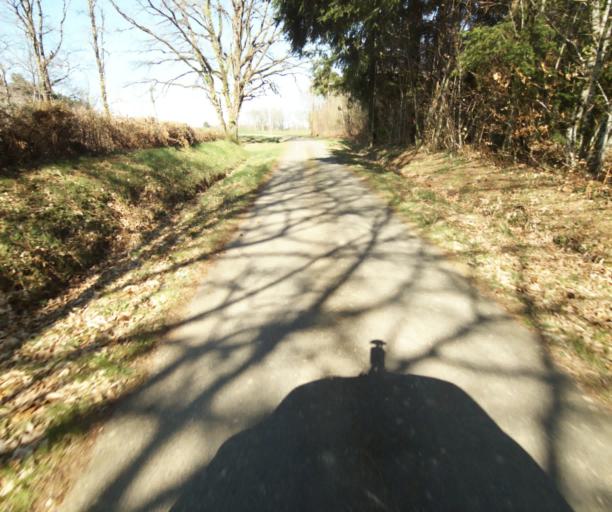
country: FR
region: Limousin
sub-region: Departement de la Correze
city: Chamboulive
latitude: 45.4313
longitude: 1.6651
